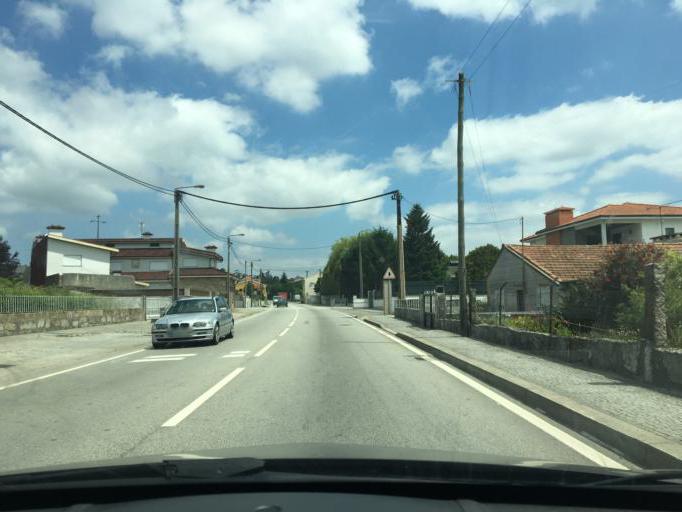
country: PT
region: Porto
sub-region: Maia
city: Anta
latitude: 41.2807
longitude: -8.6060
